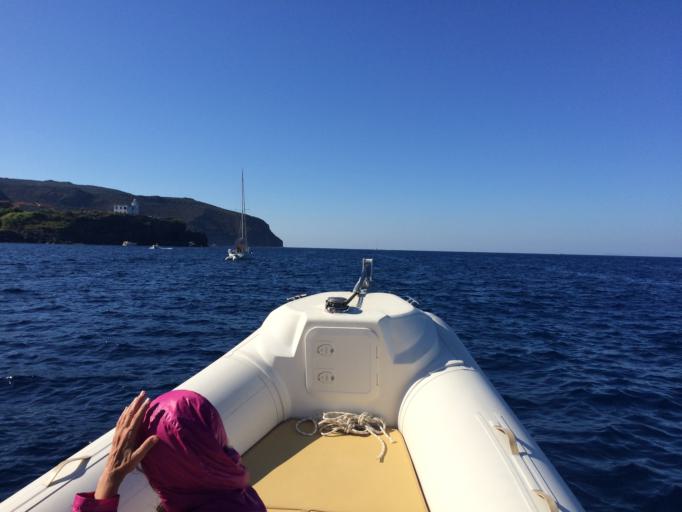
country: IT
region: Tuscany
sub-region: Provincia di Livorno
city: Capraia Isola
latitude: 43.0478
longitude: 9.8480
